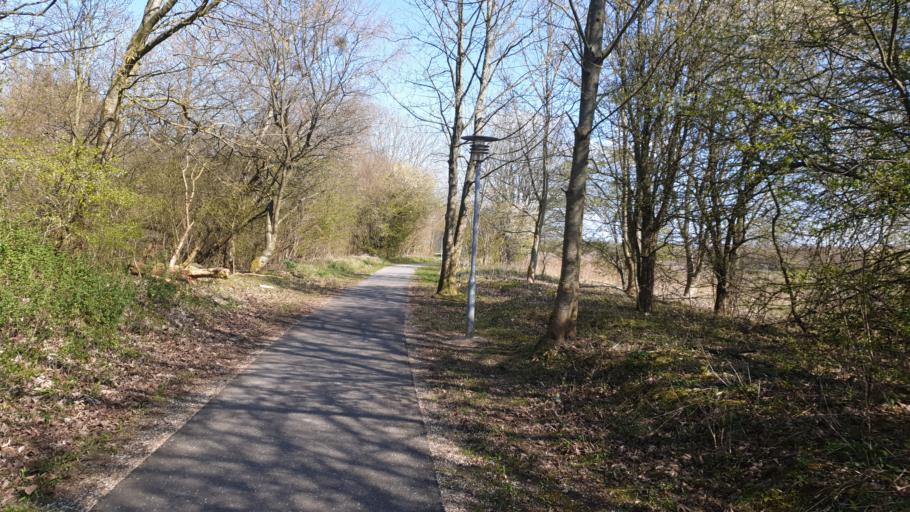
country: DK
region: Central Jutland
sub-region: Hedensted Kommune
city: Hedensted
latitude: 55.8082
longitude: 9.7036
